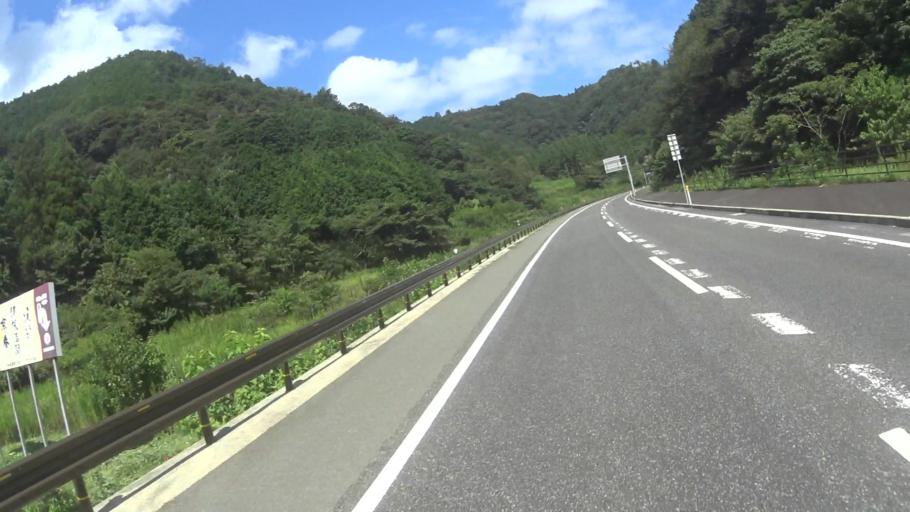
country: JP
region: Kyoto
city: Miyazu
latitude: 35.6755
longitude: 135.2738
